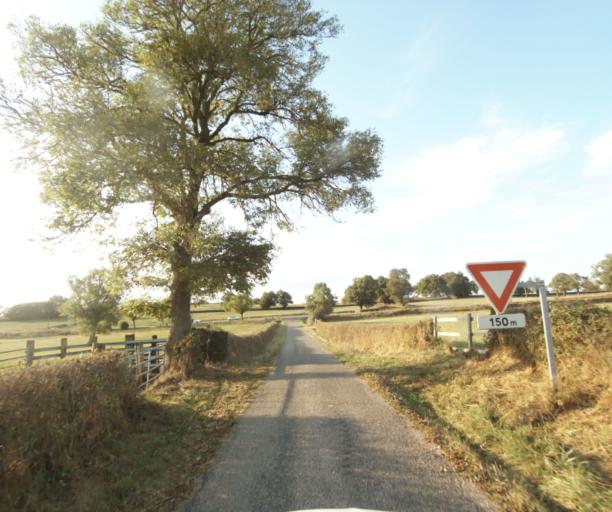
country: FR
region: Bourgogne
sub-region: Departement de Saone-et-Loire
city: Charolles
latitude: 46.4486
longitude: 4.3582
